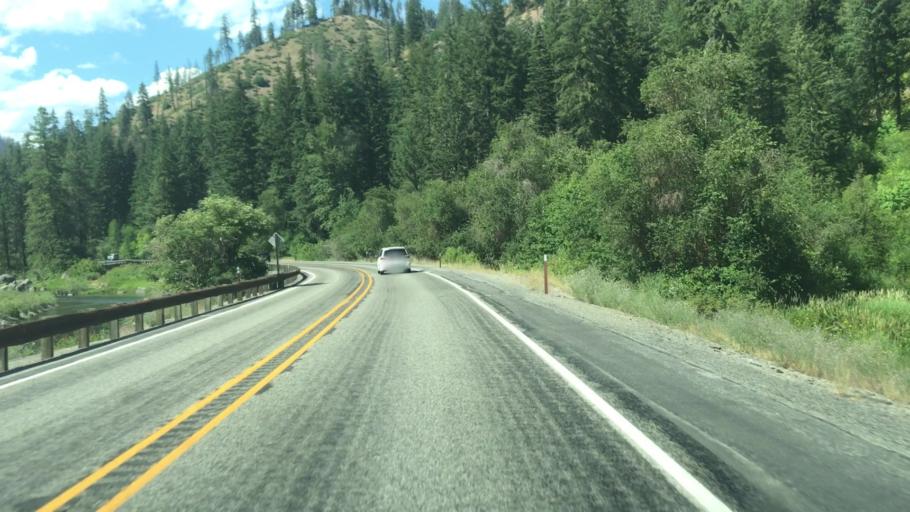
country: US
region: Washington
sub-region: Chelan County
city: Leavenworth
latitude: 47.6497
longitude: -120.7238
